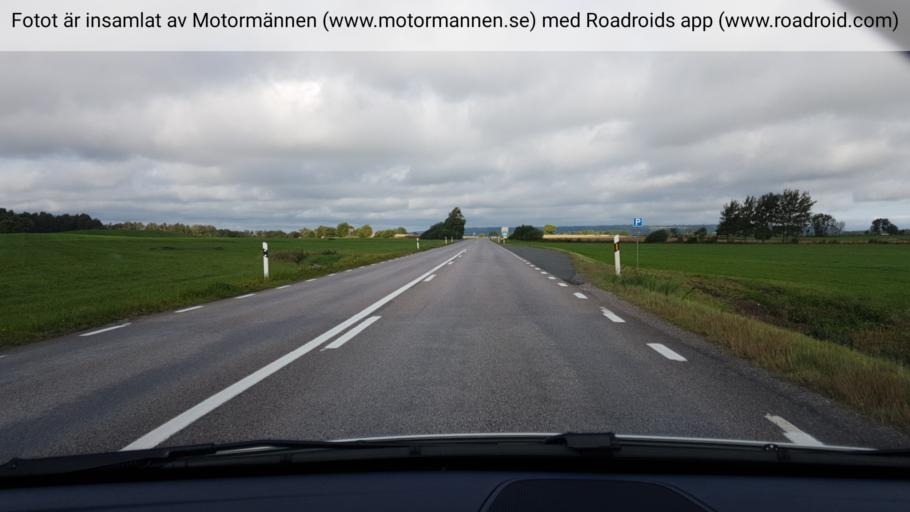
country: SE
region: Vaestra Goetaland
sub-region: Falkopings Kommun
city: Falkoeping
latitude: 58.1464
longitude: 13.6174
